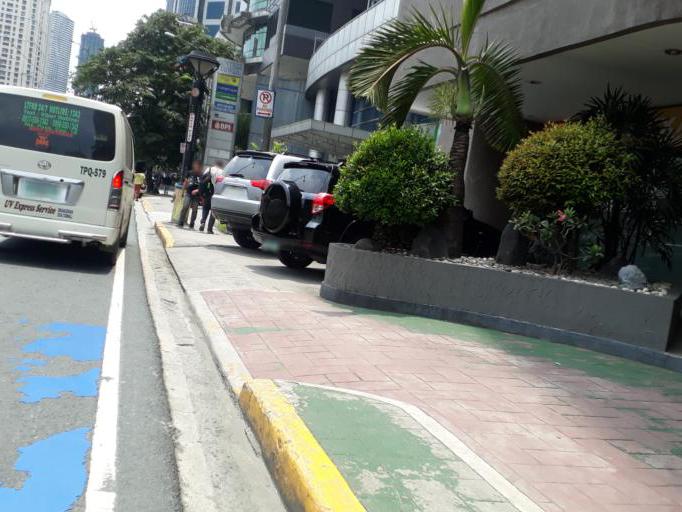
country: PH
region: Metro Manila
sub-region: Pasig
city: Pasig City
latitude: 14.5866
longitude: 121.0638
